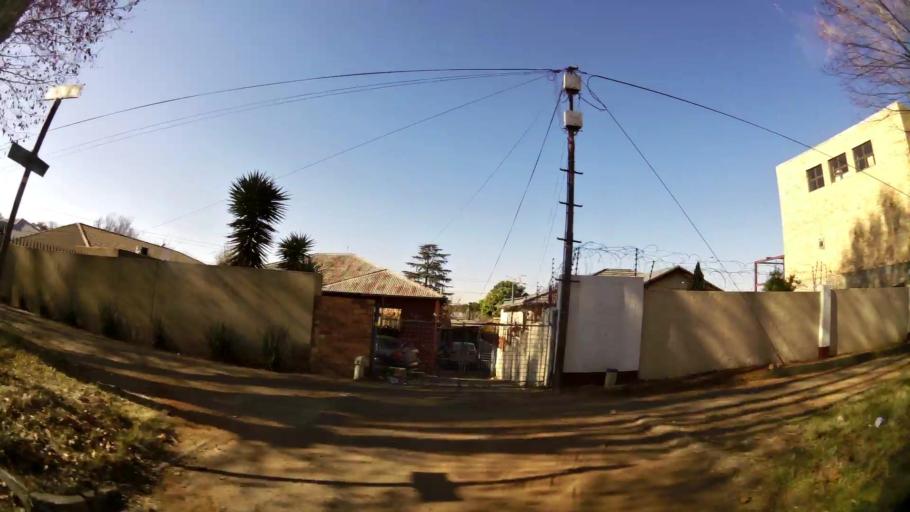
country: ZA
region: Gauteng
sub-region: City of Johannesburg Metropolitan Municipality
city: Johannesburg
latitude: -26.1985
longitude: 28.0014
